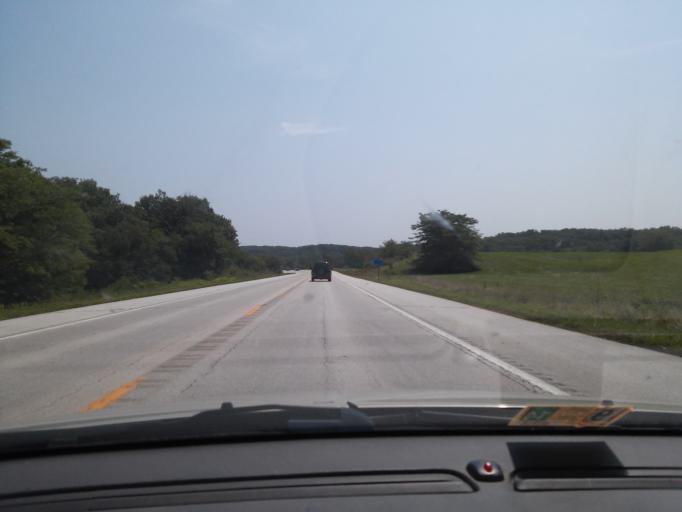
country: US
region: Missouri
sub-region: Pike County
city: Bowling Green
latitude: 39.3631
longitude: -91.1897
